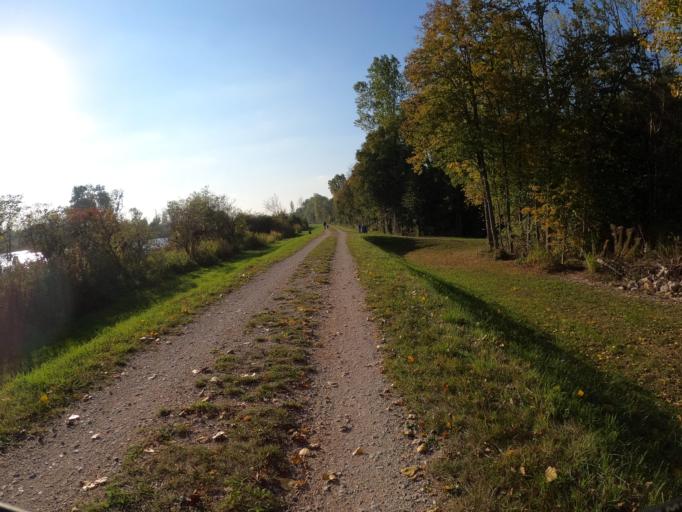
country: DE
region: Bavaria
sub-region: Swabia
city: Nersingen
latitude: 48.4450
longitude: 10.1561
